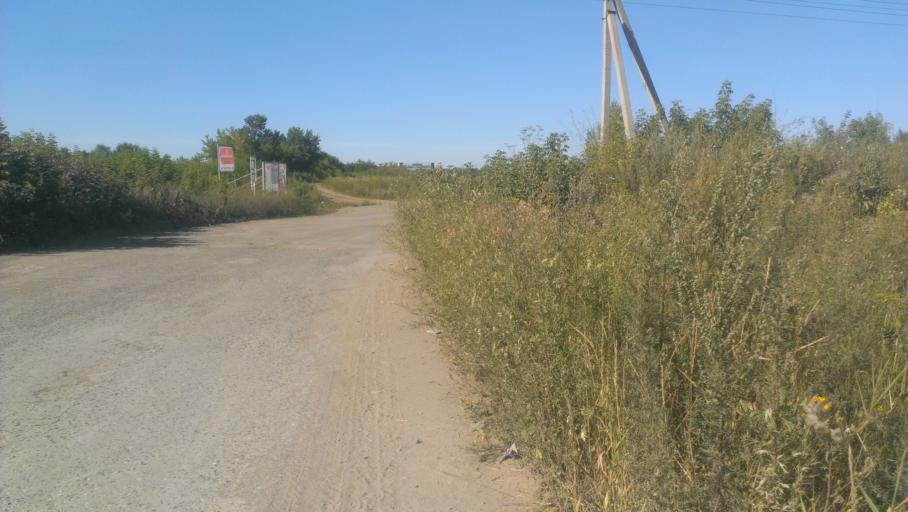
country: RU
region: Altai Krai
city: Novosilikatnyy
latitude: 53.3359
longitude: 83.6352
